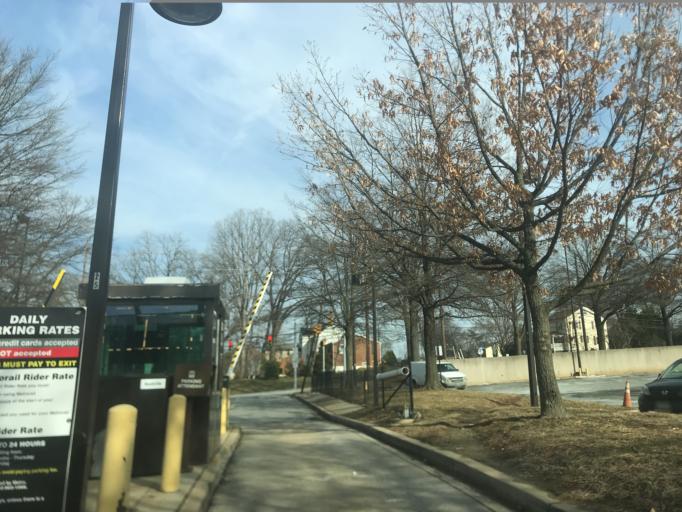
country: US
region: Maryland
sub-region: Montgomery County
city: Rockville
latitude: 39.0845
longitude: -77.1457
